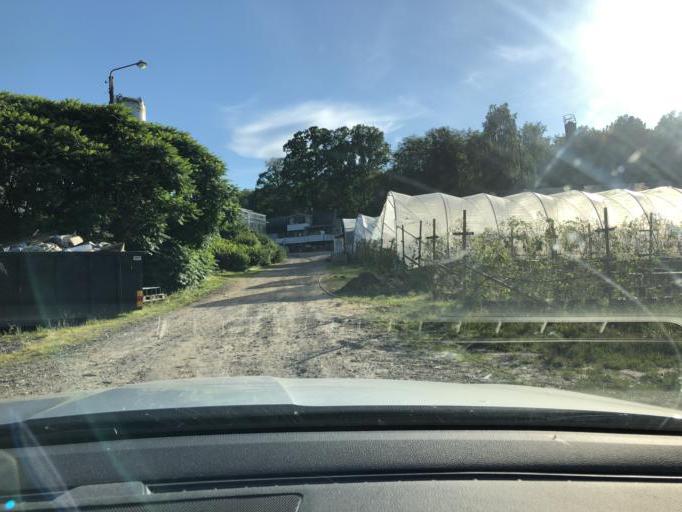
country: SE
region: Blekinge
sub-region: Solvesborgs Kommun
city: Soelvesborg
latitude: 56.1595
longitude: 14.5989
